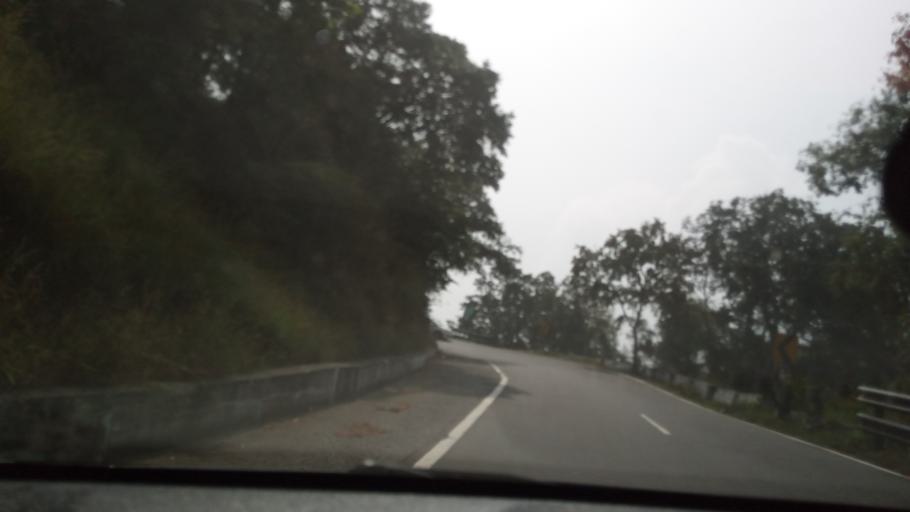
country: IN
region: Tamil Nadu
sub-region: Erode
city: Sathyamangalam
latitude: 11.6017
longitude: 77.1280
